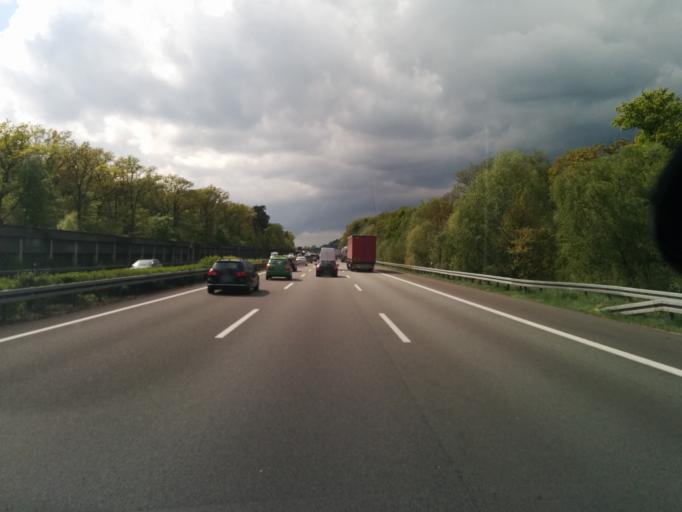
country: DE
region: Lower Saxony
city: Braunschweig
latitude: 52.3121
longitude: 10.5827
